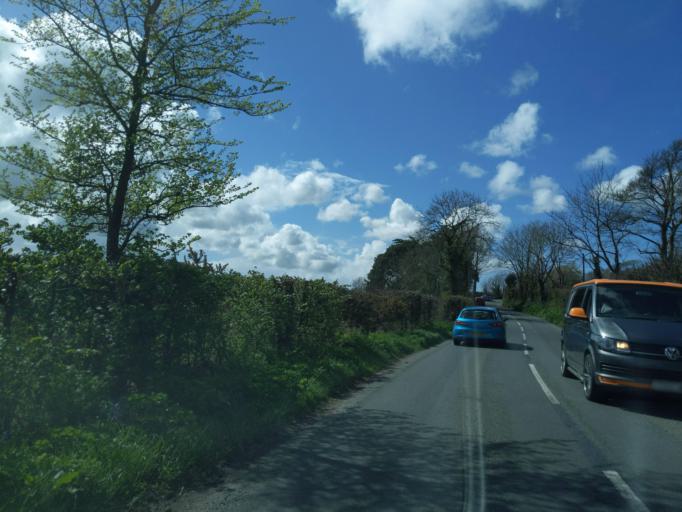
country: GB
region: England
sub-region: Cornwall
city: Wadebridge
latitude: 50.5341
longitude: -4.8443
